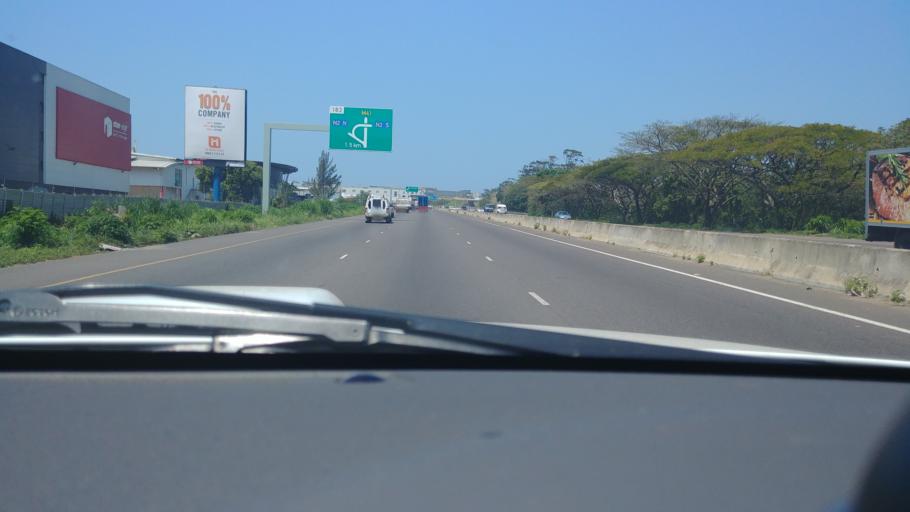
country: ZA
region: KwaZulu-Natal
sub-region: eThekwini Metropolitan Municipality
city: Durban
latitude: -29.7075
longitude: 31.0442
